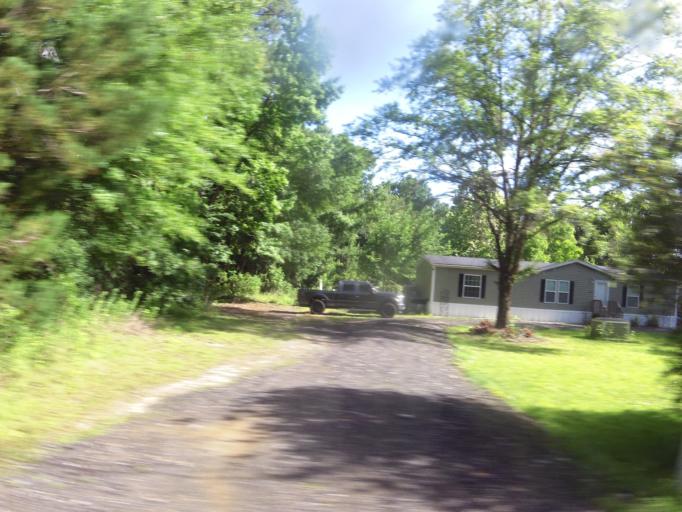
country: US
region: Florida
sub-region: Nassau County
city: Callahan
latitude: 30.5611
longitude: -81.8140
